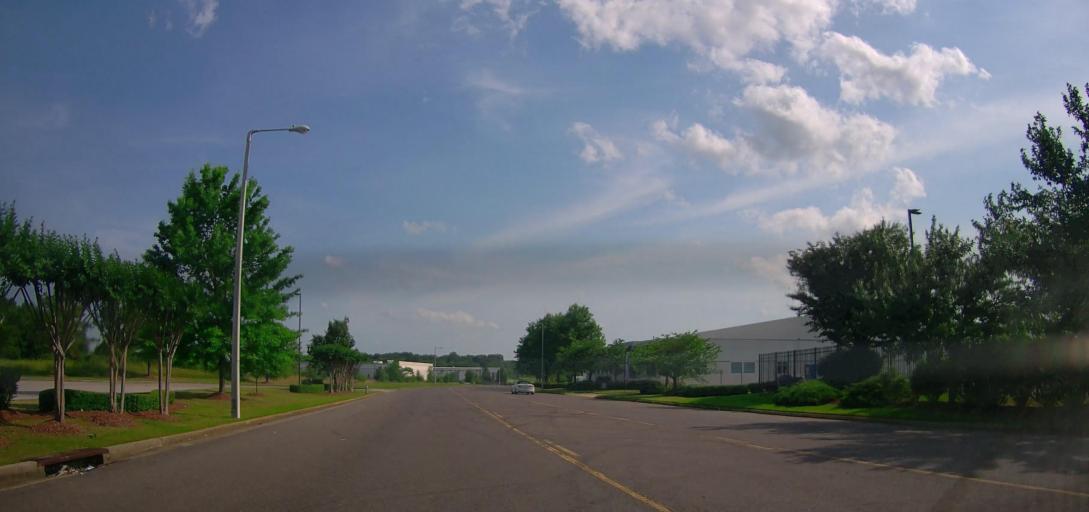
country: US
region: Mississippi
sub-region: De Soto County
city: Olive Branch
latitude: 35.0013
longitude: -89.8603
